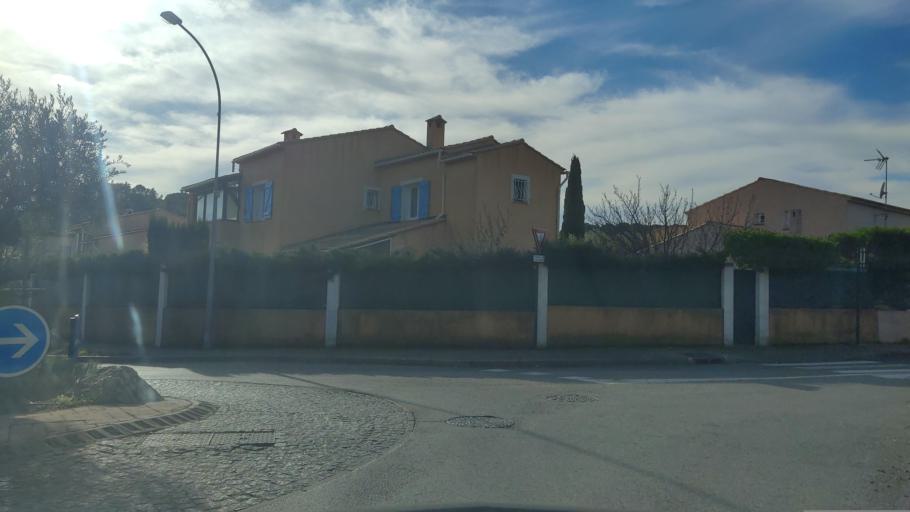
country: FR
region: Provence-Alpes-Cote d'Azur
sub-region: Departement du Var
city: Sanary-sur-Mer
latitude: 43.1262
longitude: 5.8010
